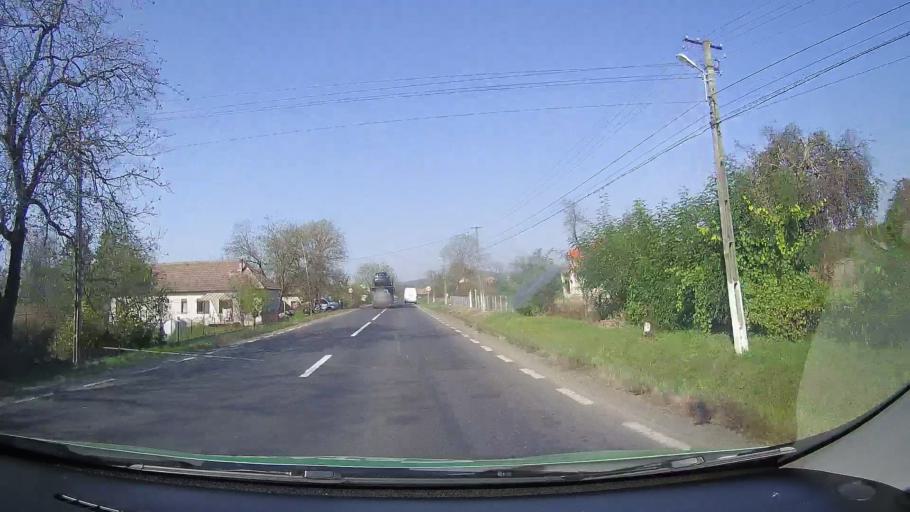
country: RO
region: Arad
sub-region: Comuna Varadia de Mures
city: Varadia de Mures
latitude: 46.0079
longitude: 22.1519
